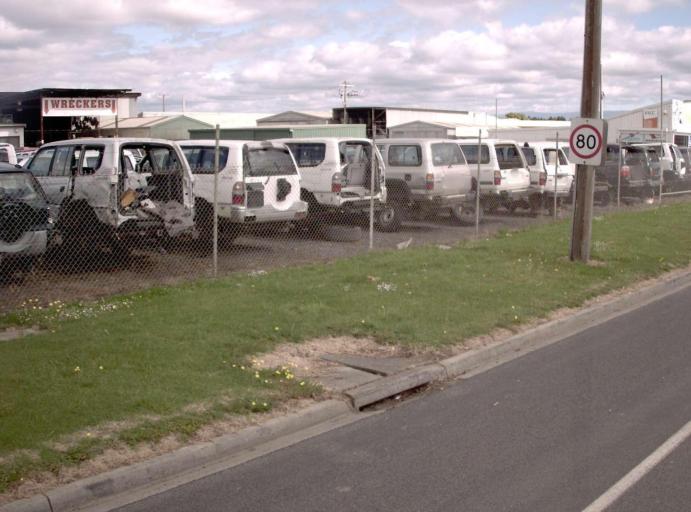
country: AU
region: Victoria
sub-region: Latrobe
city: Morwell
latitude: -38.2251
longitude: 146.4426
